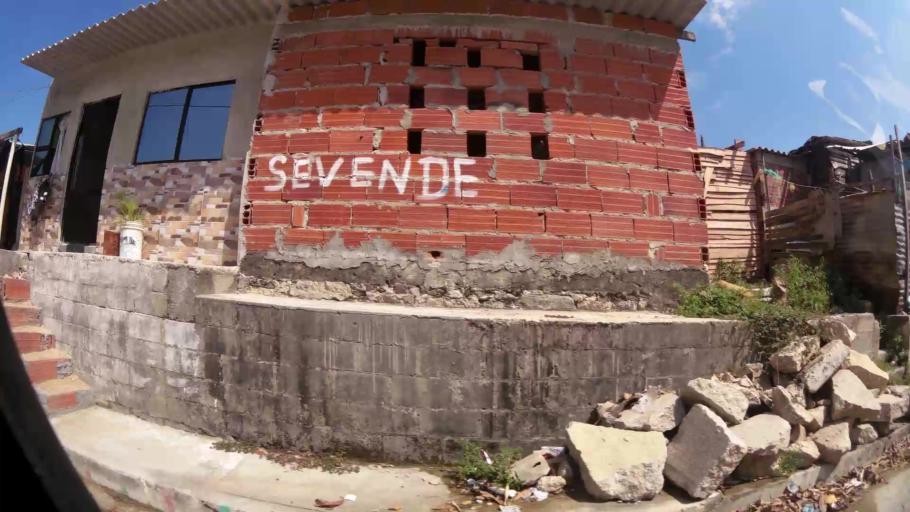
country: CO
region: Atlantico
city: Barranquilla
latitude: 10.9610
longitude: -74.8224
